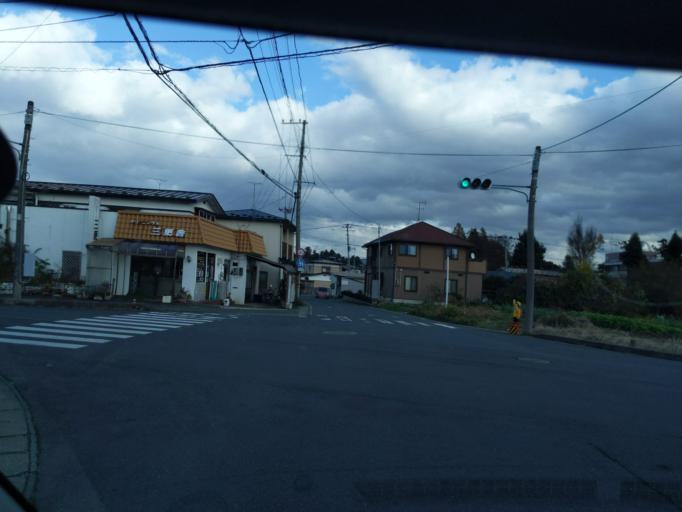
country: JP
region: Iwate
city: Mizusawa
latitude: 39.1358
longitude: 141.1311
